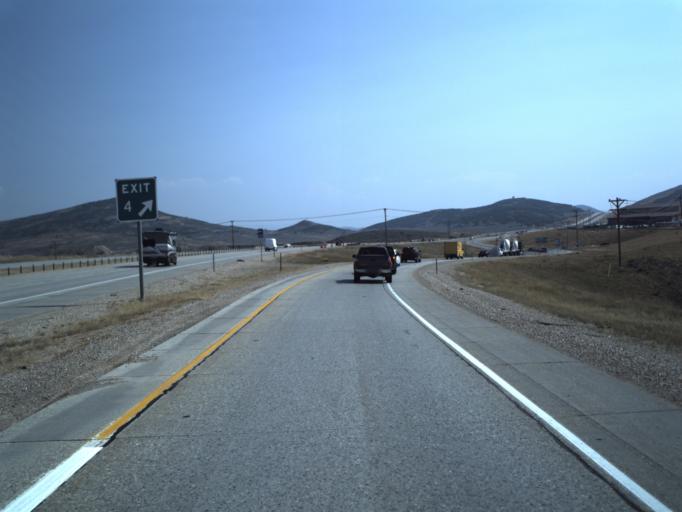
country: US
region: Utah
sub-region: Summit County
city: Park City
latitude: 40.6866
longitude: -111.4645
